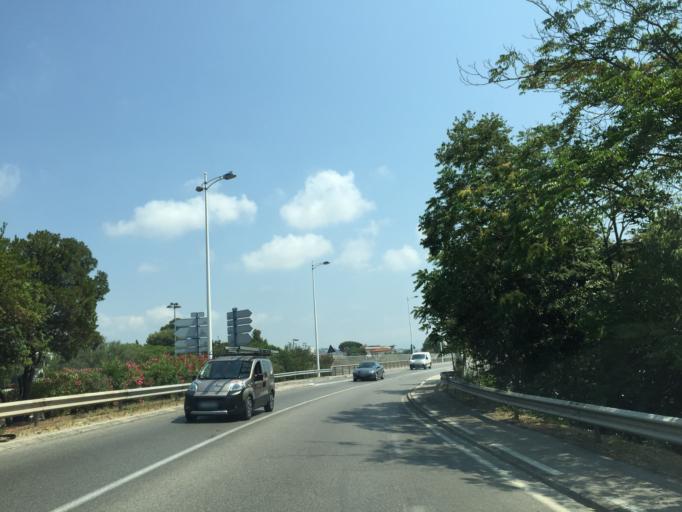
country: FR
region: Provence-Alpes-Cote d'Azur
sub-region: Departement des Alpes-Maritimes
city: Cagnes-sur-Mer
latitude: 43.6525
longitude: 7.1433
